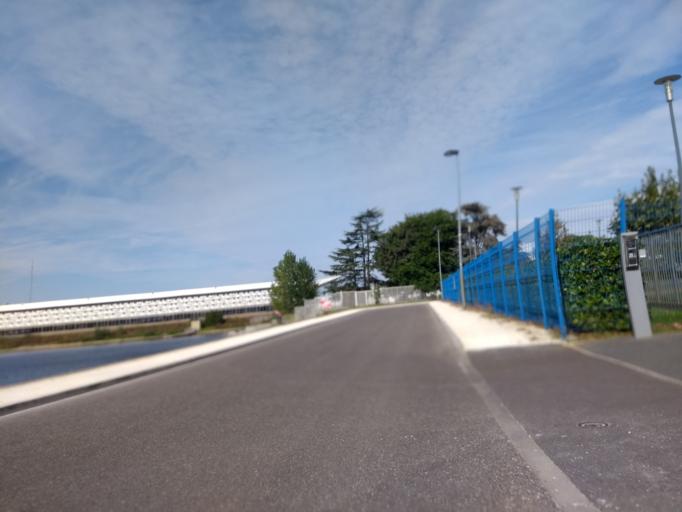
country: FR
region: Aquitaine
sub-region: Departement de la Gironde
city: Le Bouscat
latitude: 44.8909
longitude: -0.5670
